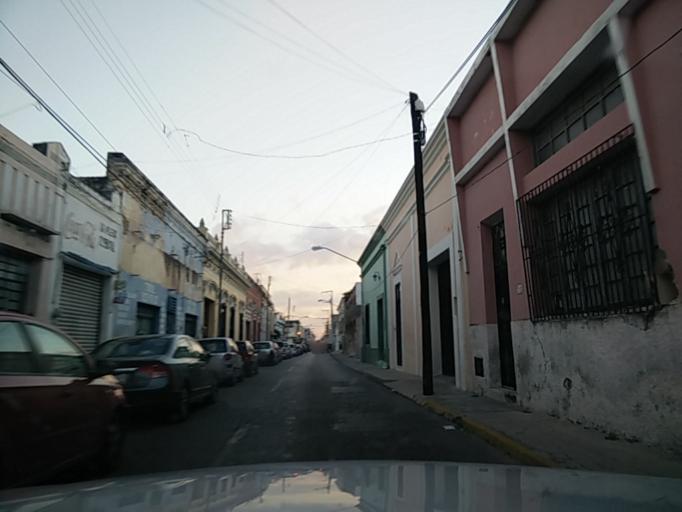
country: MX
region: Yucatan
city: Merida
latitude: 20.9726
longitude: -89.6261
